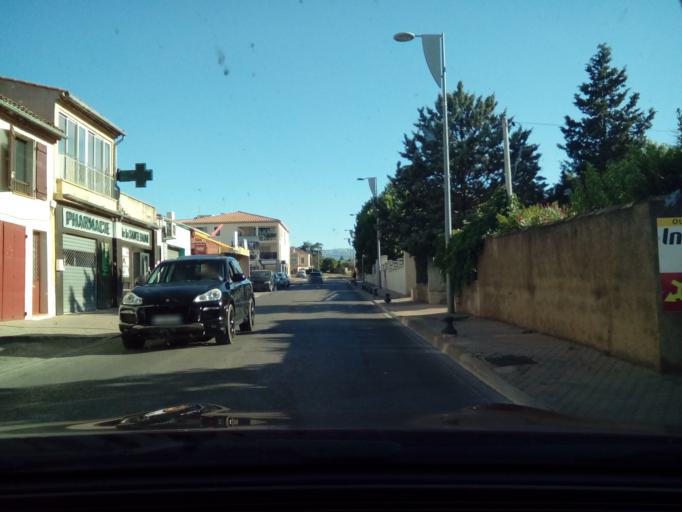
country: FR
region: Provence-Alpes-Cote d'Azur
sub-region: Departement du Var
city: Saint-Maximin-la-Sainte-Baume
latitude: 43.4502
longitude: 5.8617
